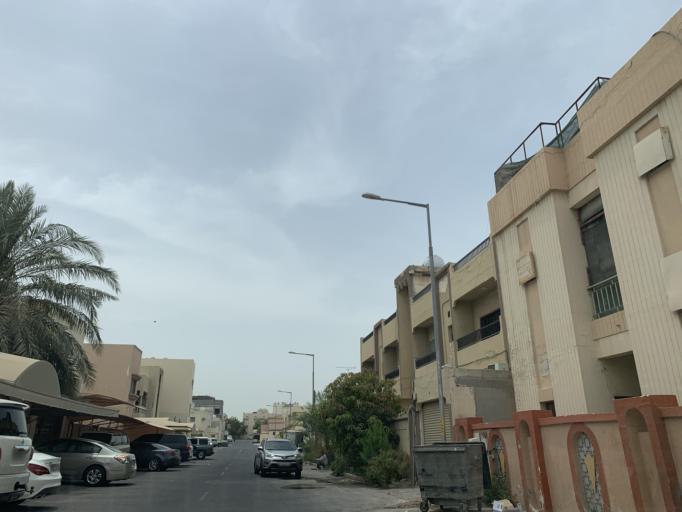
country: BH
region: Northern
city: Ar Rifa'
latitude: 26.1339
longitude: 50.5680
